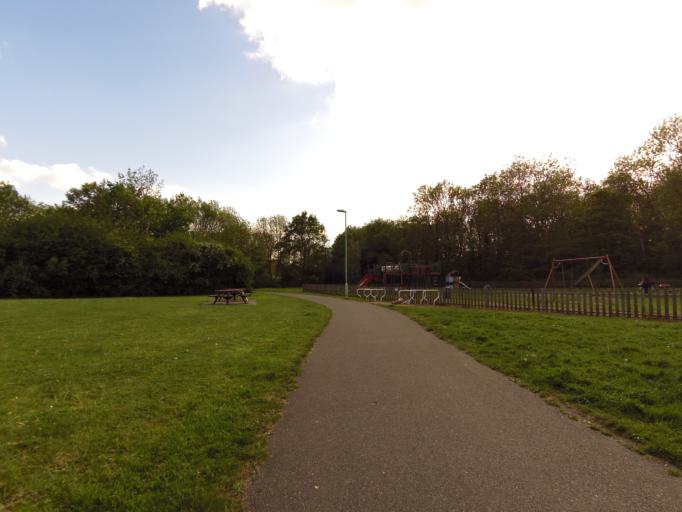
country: GB
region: England
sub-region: Suffolk
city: Beccles
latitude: 52.4488
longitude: 1.5914
